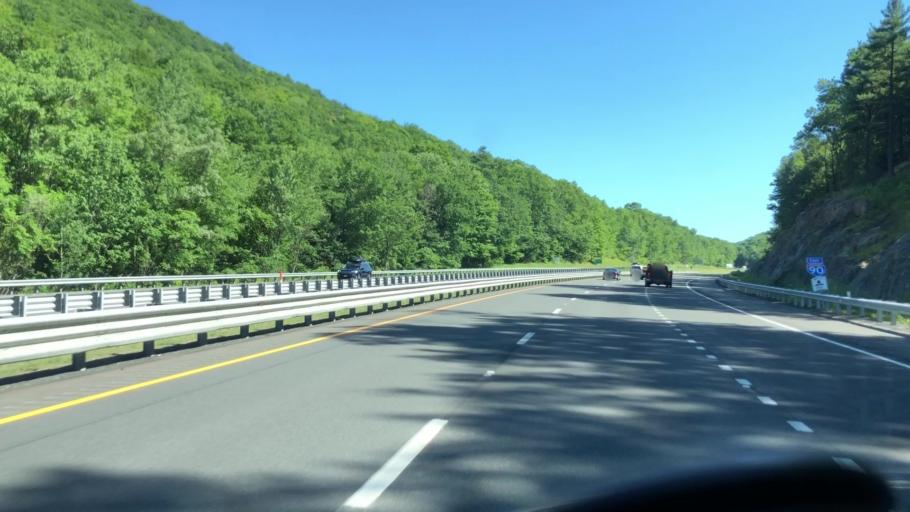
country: US
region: Massachusetts
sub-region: Berkshire County
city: West Stockbridge
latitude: 42.3207
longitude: -73.3592
